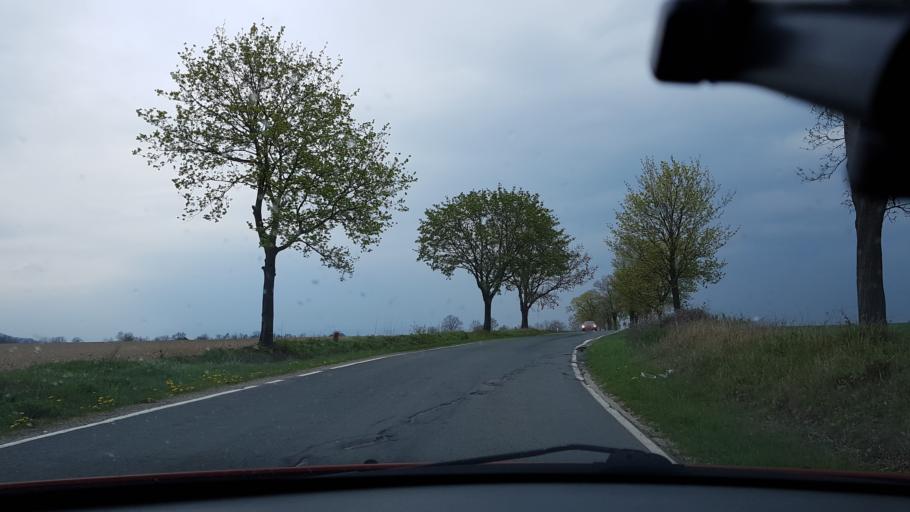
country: PL
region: Lower Silesian Voivodeship
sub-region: Powiat klodzki
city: Bystrzyca Klodzka
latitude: 50.3353
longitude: 16.5966
